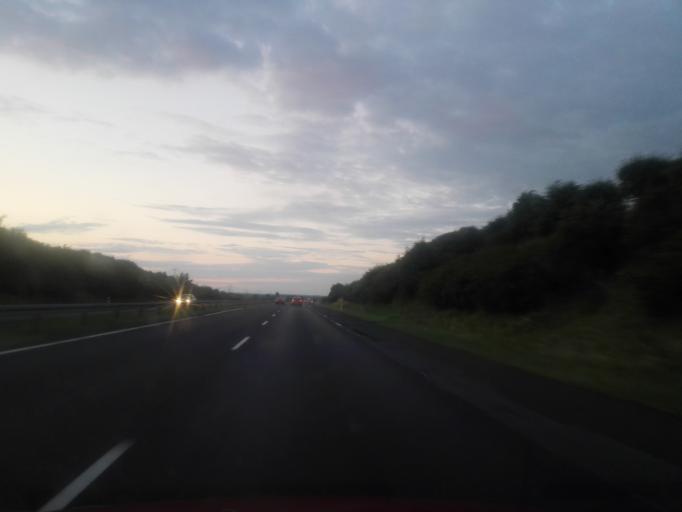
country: PL
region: Lodz Voivodeship
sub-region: Powiat radomszczanski
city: Kamiensk
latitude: 51.1950
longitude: 19.4745
